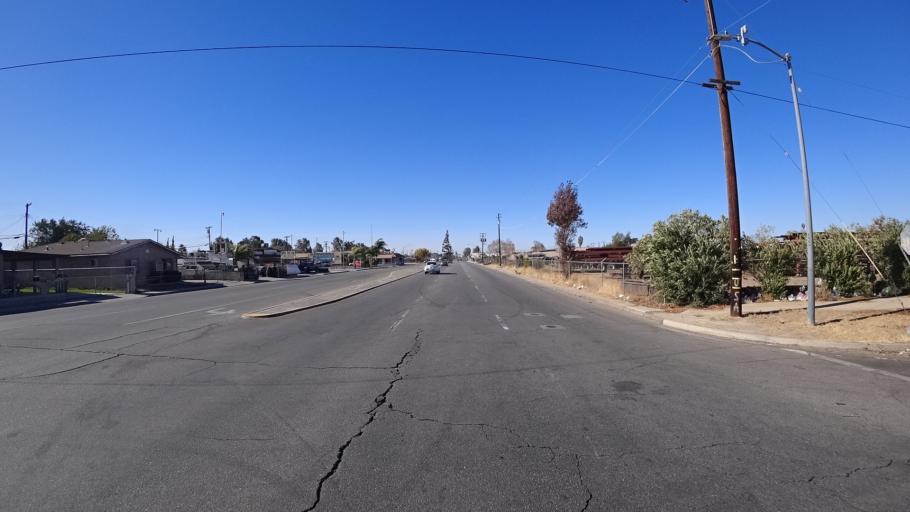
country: US
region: California
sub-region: Kern County
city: Bakersfield
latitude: 35.3686
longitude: -118.9804
